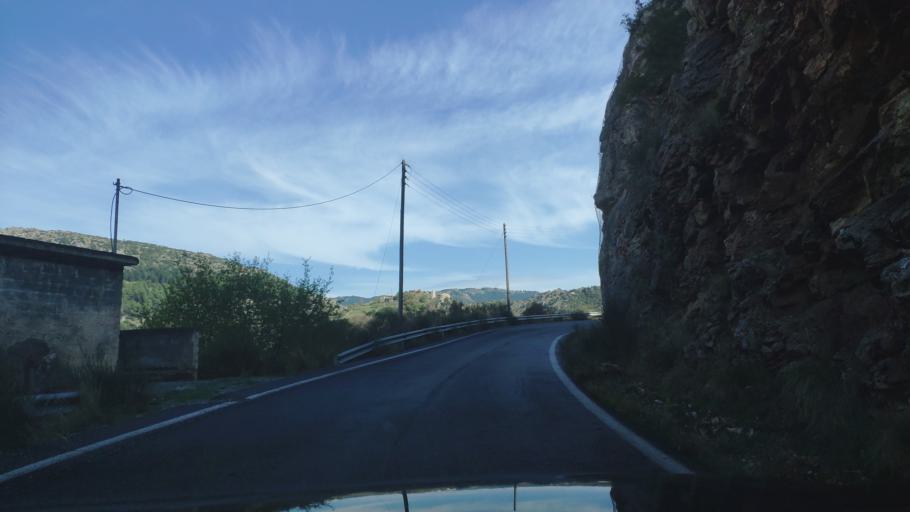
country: GR
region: Peloponnese
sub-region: Nomos Arkadias
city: Dimitsana
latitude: 37.5978
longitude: 22.0297
